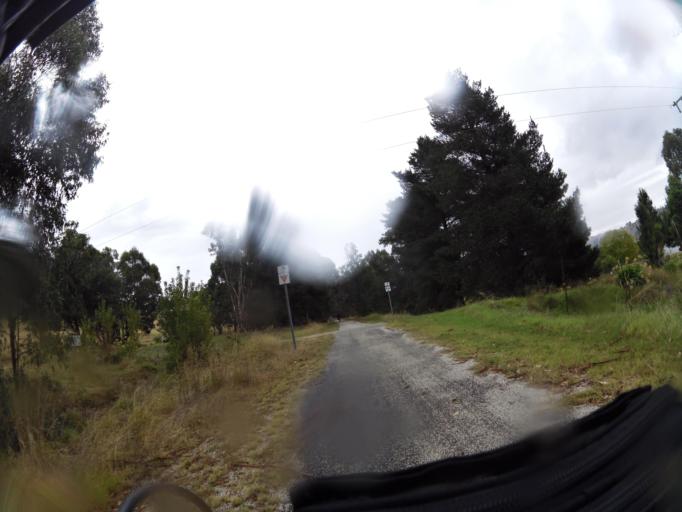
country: AU
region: New South Wales
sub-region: Albury Municipality
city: East Albury
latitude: -36.2162
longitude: 147.2233
